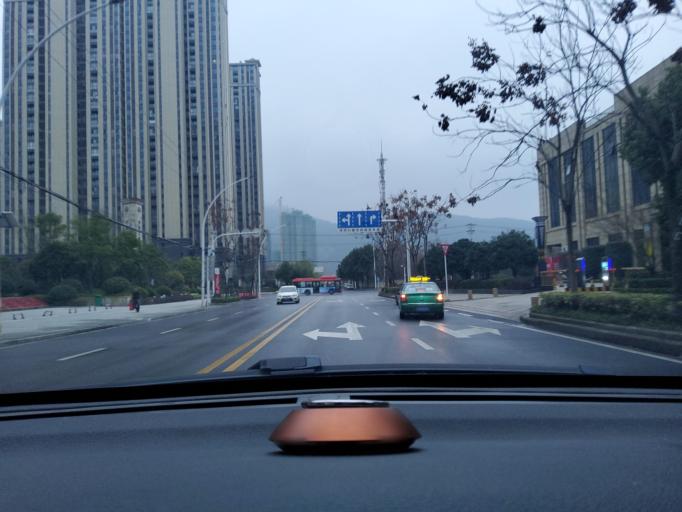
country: CN
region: Hubei
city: Tuanchengshan
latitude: 30.1961
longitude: 115.0094
